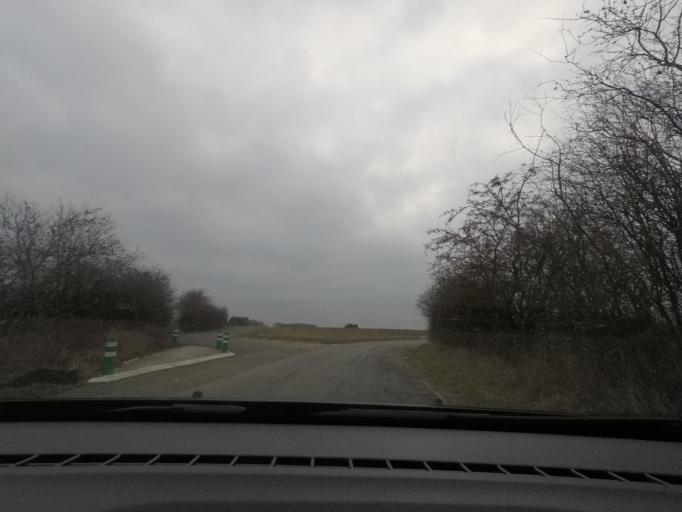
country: BE
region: Wallonia
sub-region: Province du Luxembourg
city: Habay-la-Vieille
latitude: 49.7145
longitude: 5.5860
